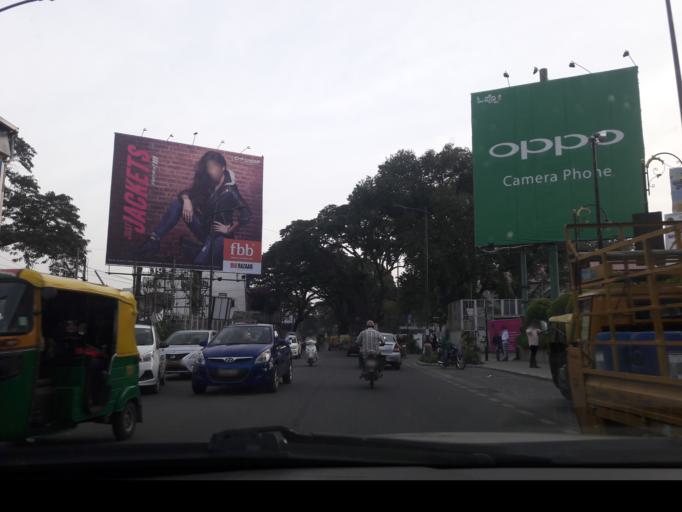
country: IN
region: Karnataka
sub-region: Bangalore Urban
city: Bangalore
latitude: 12.9698
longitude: 77.6104
